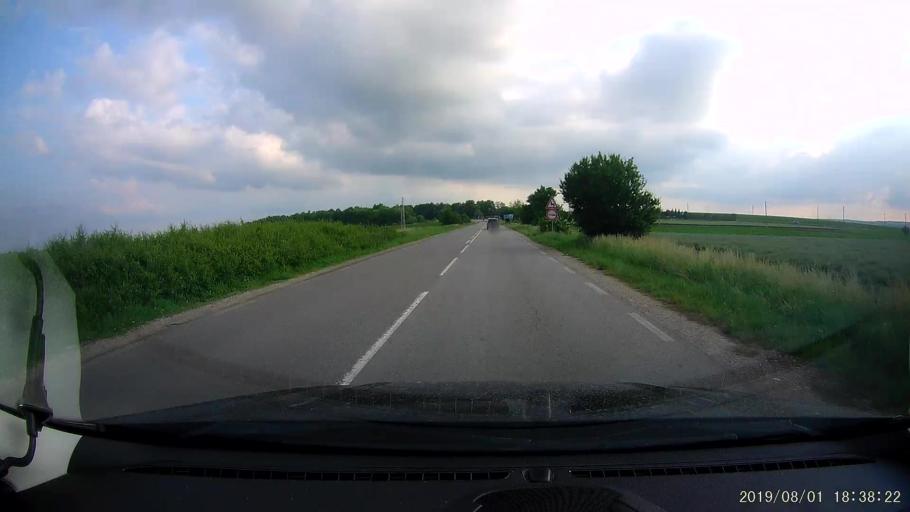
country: BG
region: Shumen
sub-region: Obshtina Khitrino
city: Gara Khitrino
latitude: 43.4031
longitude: 26.9176
